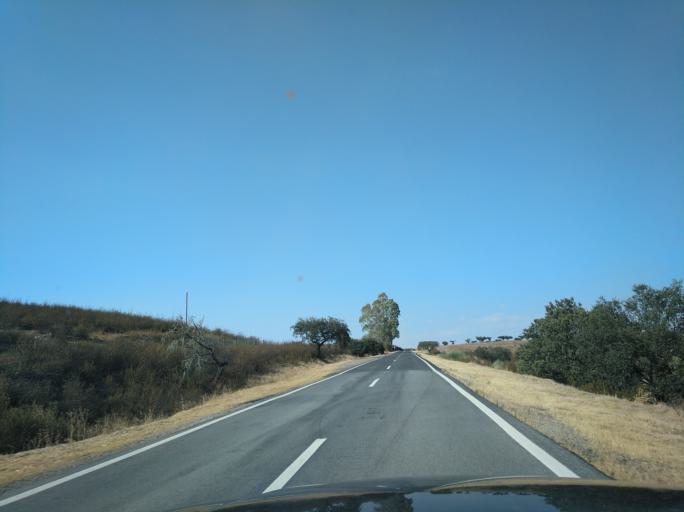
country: ES
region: Extremadura
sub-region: Provincia de Badajoz
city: Valencia del Mombuey
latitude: 38.1554
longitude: -7.2339
